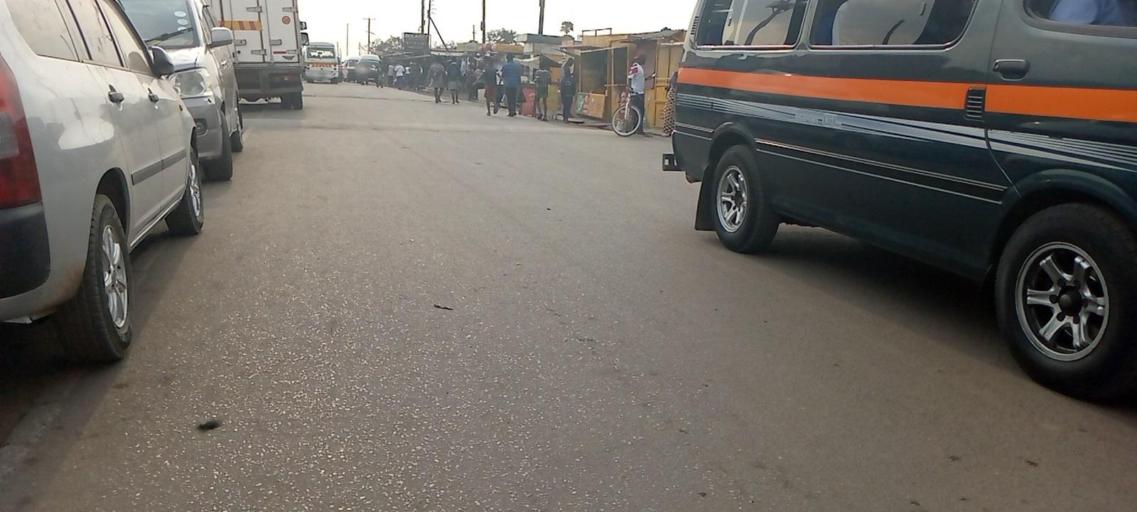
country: ZM
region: Lusaka
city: Lusaka
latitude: -15.4022
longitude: 28.3549
